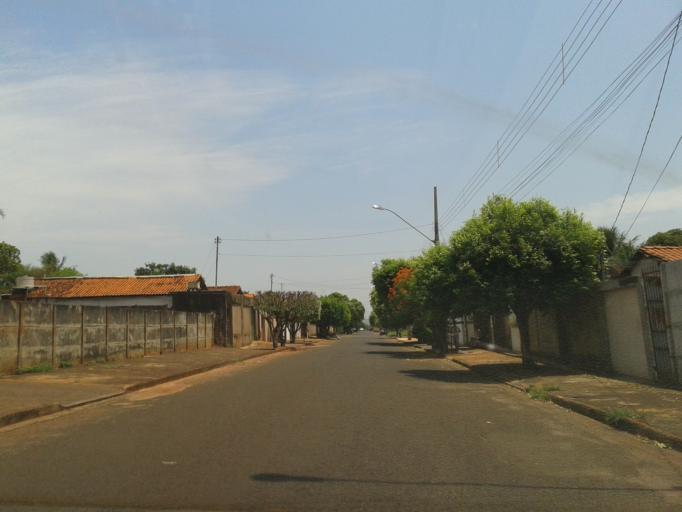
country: BR
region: Minas Gerais
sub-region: Ituiutaba
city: Ituiutaba
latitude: -18.9899
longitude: -49.4450
